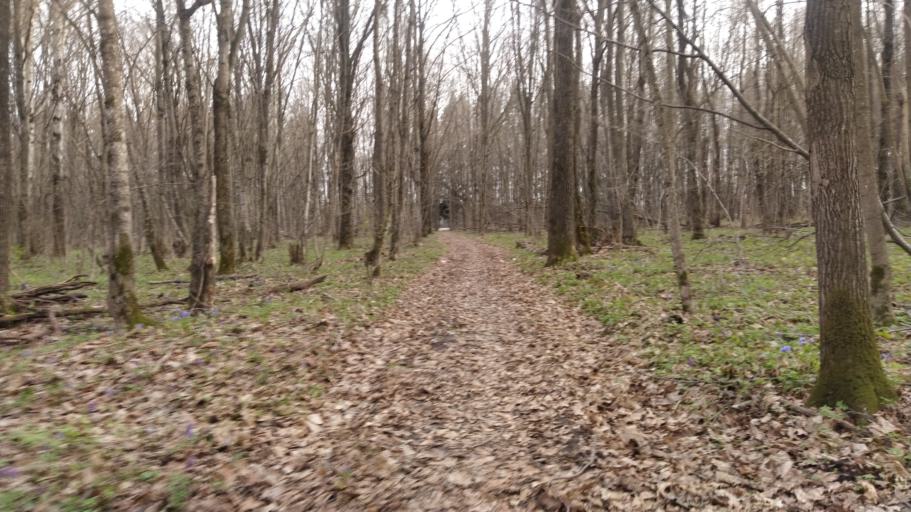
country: RU
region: Chuvashia
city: Novyye Lapsary
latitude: 56.1295
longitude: 47.1219
